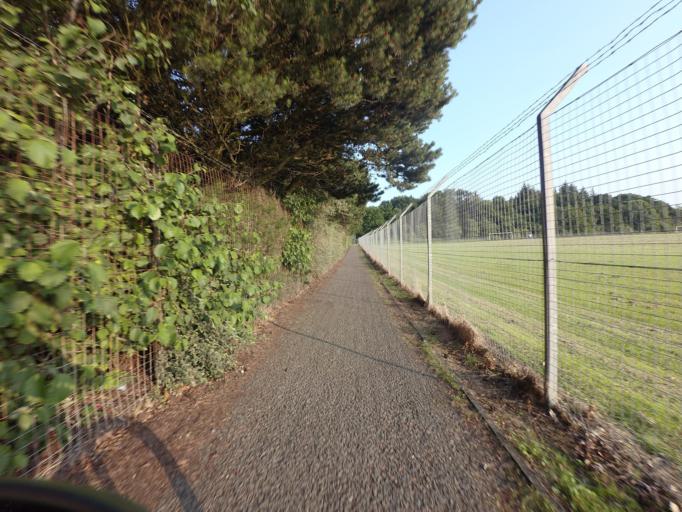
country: GB
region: Scotland
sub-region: West Lothian
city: Livingston
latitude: 55.9021
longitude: -3.5063
